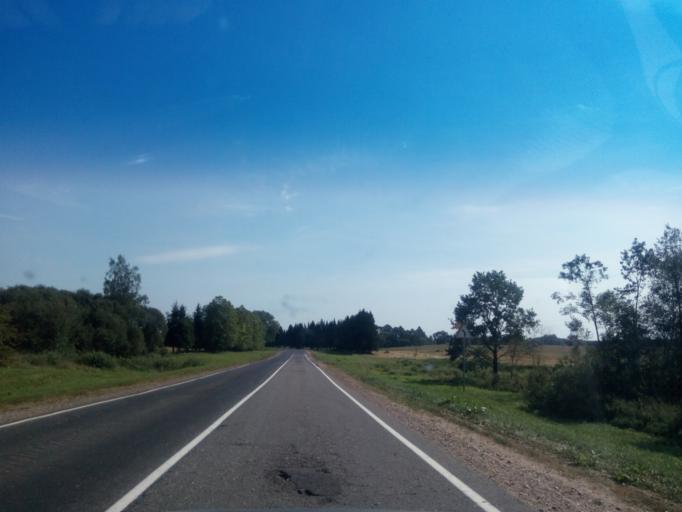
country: BY
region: Vitebsk
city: Vyerkhnyadzvinsk
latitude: 55.7334
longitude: 27.9975
